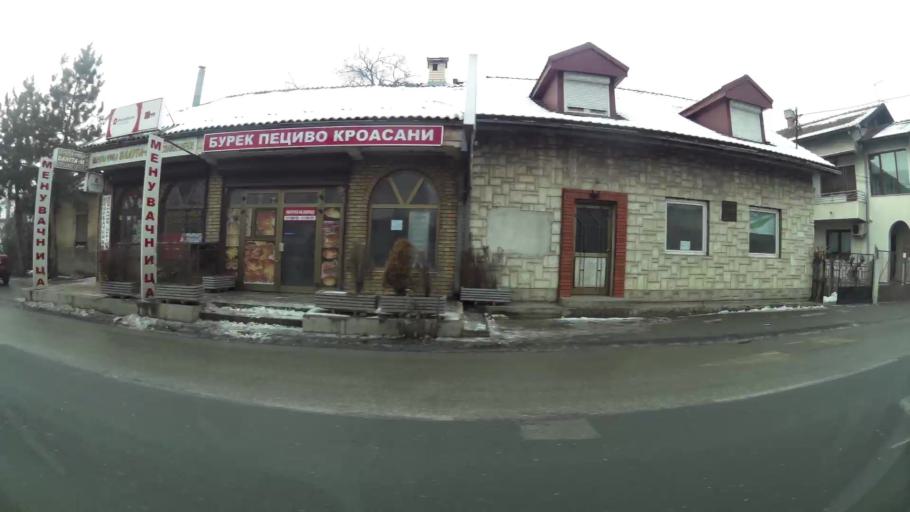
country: MK
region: Kisela Voda
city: Kisela Voda
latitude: 41.9962
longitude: 21.4989
